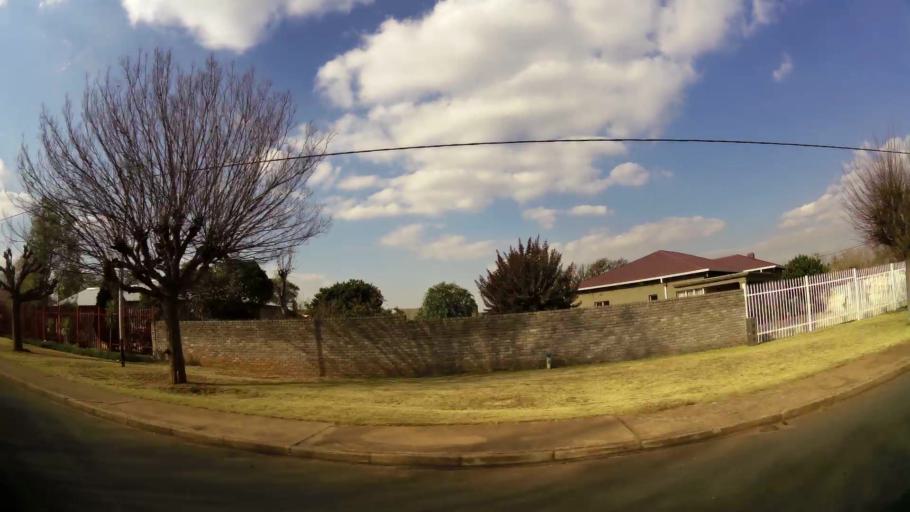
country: ZA
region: Gauteng
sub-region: West Rand District Municipality
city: Krugersdorp
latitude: -26.0855
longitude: 27.7727
